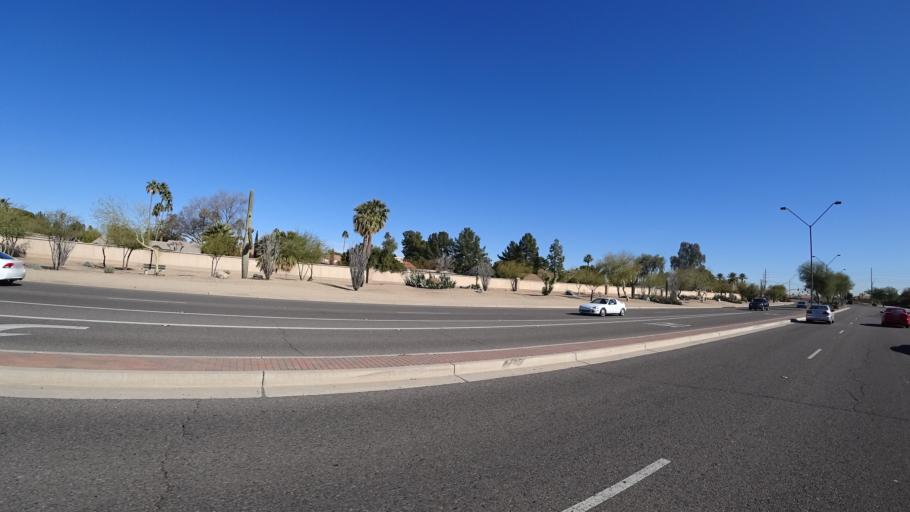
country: US
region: Arizona
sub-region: Maricopa County
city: Litchfield Park
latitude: 33.4857
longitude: -112.3611
